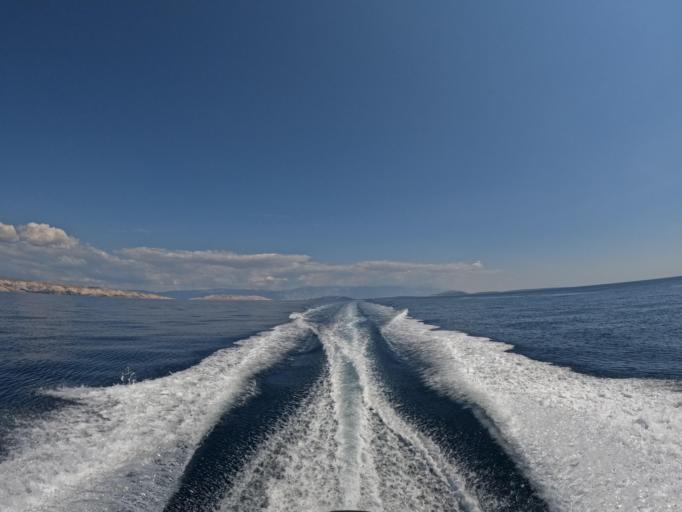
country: HR
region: Primorsko-Goranska
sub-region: Grad Krk
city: Krk
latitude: 44.9190
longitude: 14.5702
